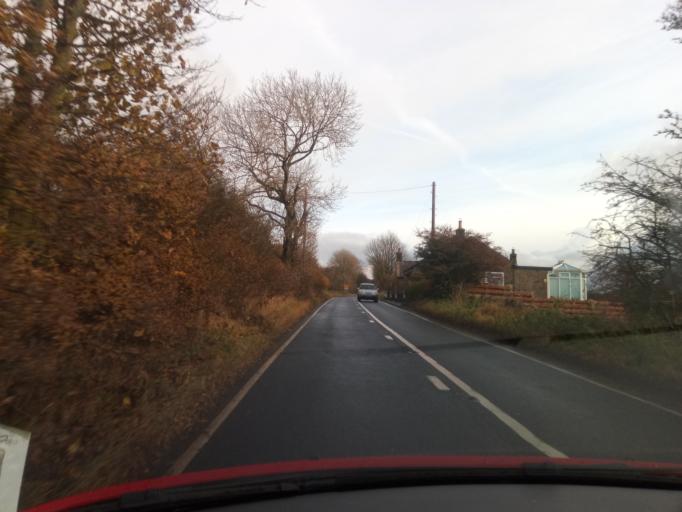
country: GB
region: England
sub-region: Northumberland
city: Acomb
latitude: 55.0191
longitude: -2.1021
